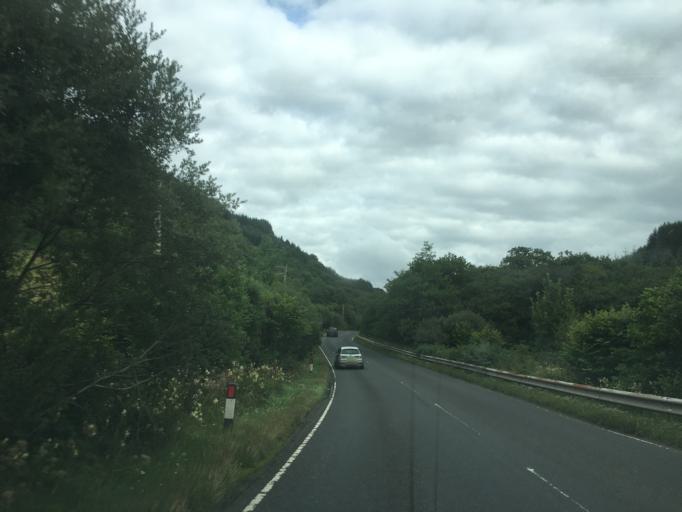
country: GB
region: Scotland
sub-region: Argyll and Bute
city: Oban
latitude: 56.3176
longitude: -5.4886
